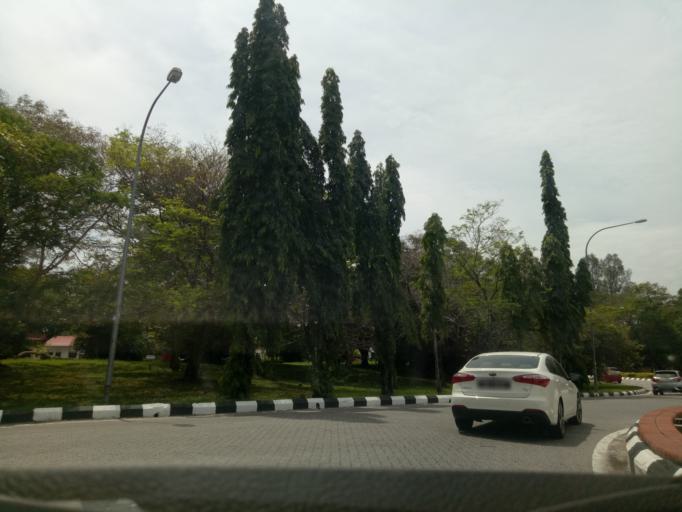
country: MY
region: Perak
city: Ipoh
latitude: 4.5979
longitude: 101.1052
